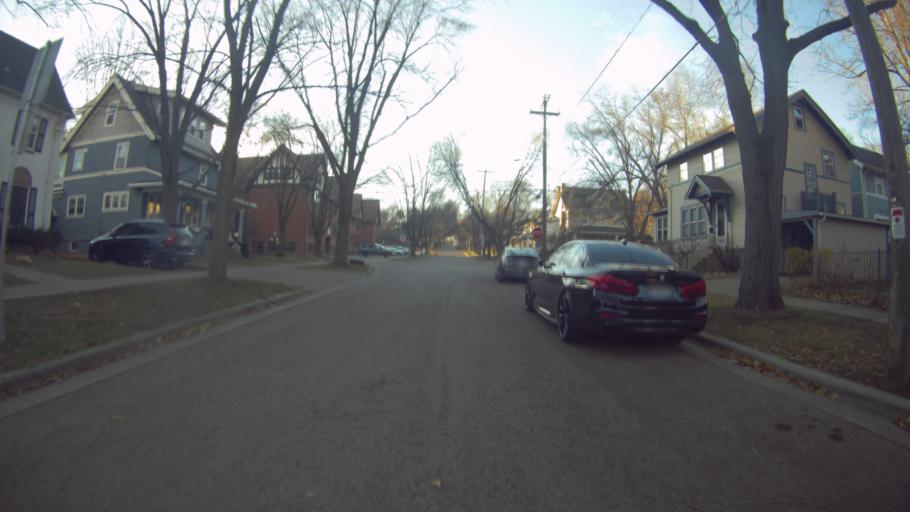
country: US
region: Wisconsin
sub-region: Dane County
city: Madison
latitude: 43.0687
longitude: -89.4163
